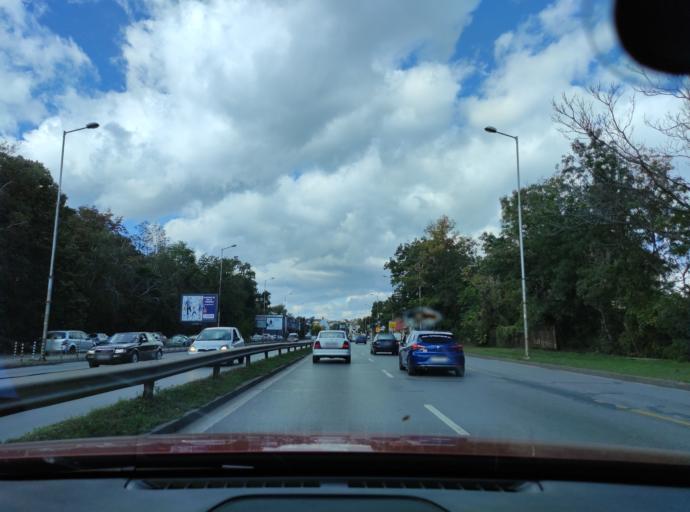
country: BG
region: Sofia-Capital
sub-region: Stolichna Obshtina
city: Sofia
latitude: 42.7027
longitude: 23.3377
